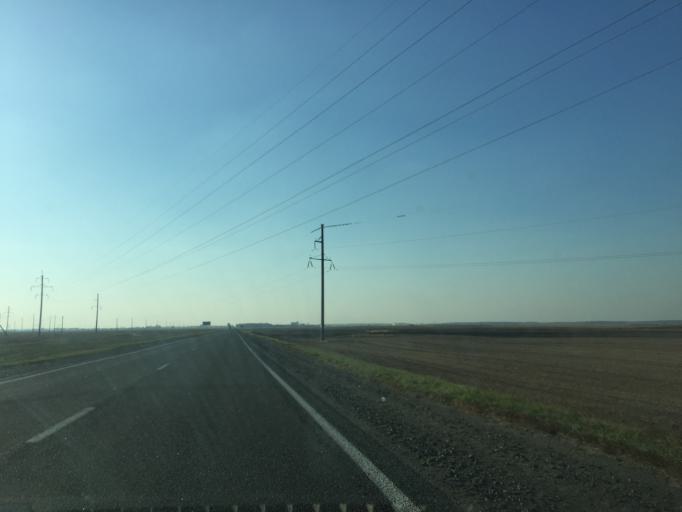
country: BY
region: Gomel
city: Dobrush
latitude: 52.3861
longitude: 31.4243
